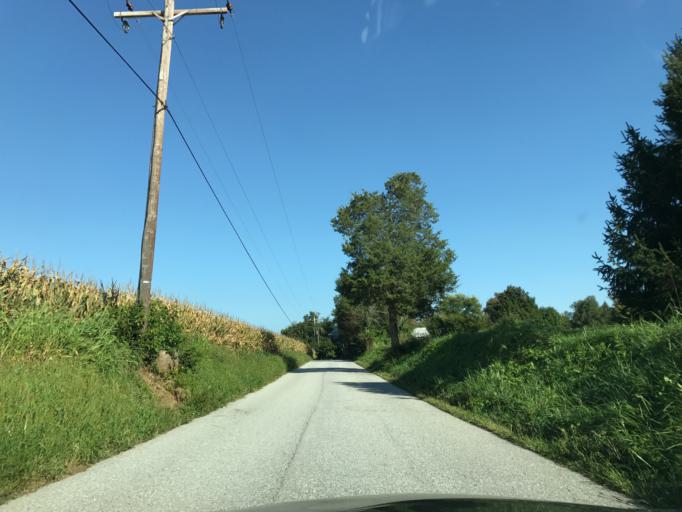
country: US
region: Maryland
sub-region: Harford County
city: Jarrettsville
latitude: 39.6060
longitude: -76.5796
